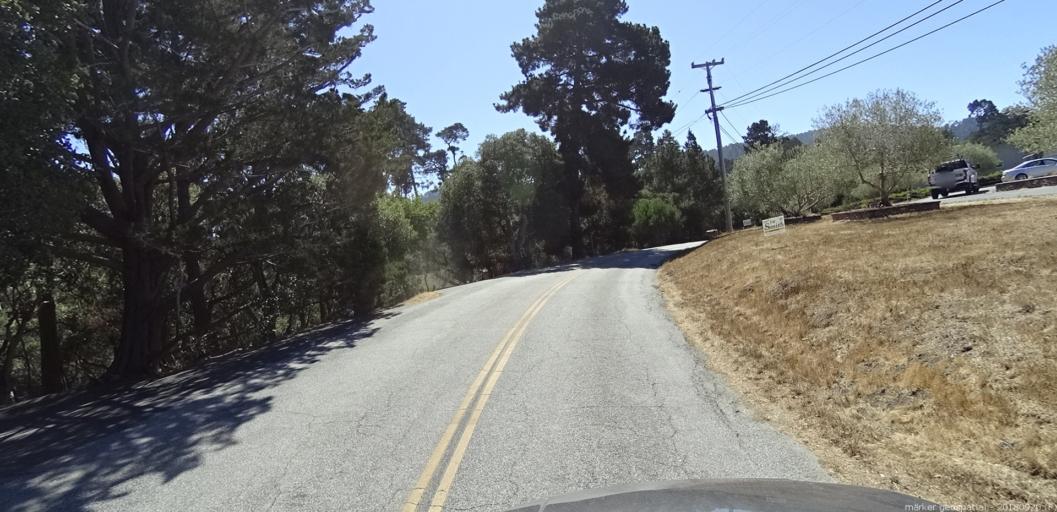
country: US
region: California
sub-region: Monterey County
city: Monterey
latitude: 36.5815
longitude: -121.8679
